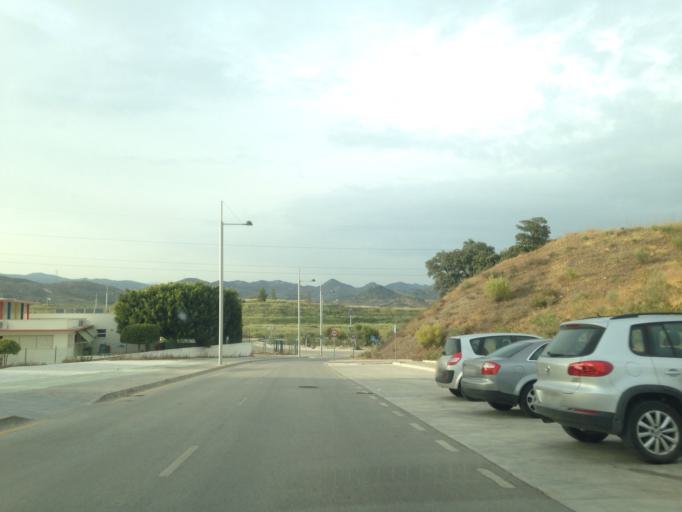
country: ES
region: Andalusia
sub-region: Provincia de Malaga
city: Estacion de Cartama
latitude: 36.7379
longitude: -4.5468
